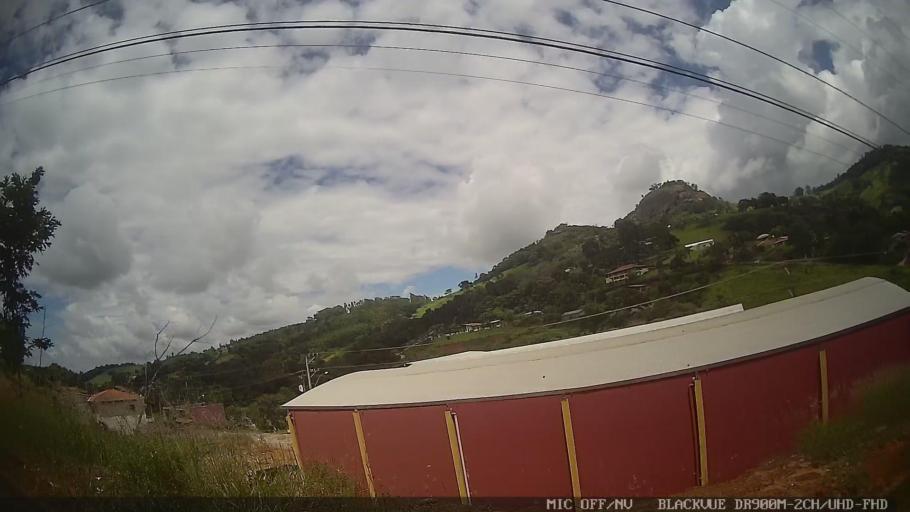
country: BR
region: Minas Gerais
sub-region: Extrema
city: Extrema
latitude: -22.7881
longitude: -46.4431
